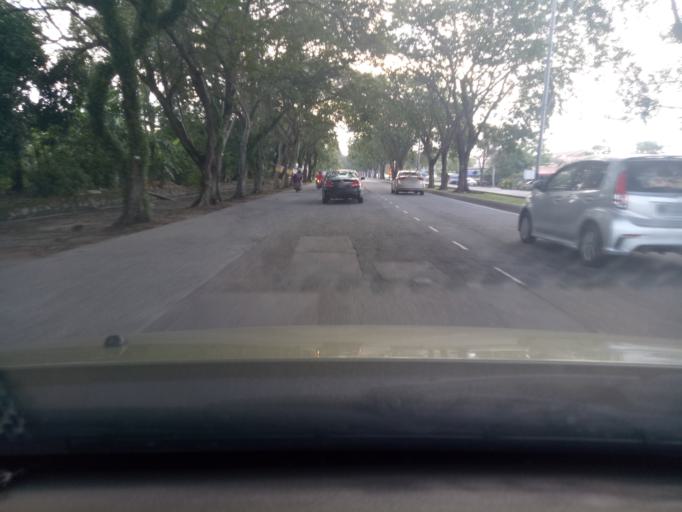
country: MY
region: Kedah
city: Alor Setar
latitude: 6.1429
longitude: 100.3615
